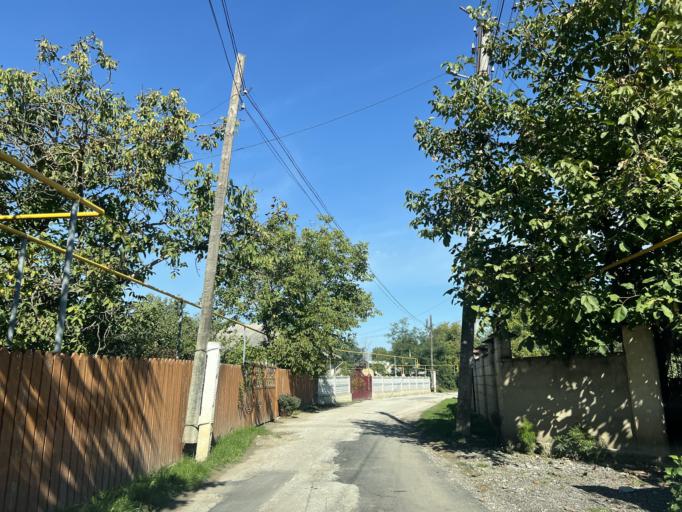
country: RO
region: Iasi
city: Ungheni-Prut
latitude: 47.1964
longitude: 27.7884
